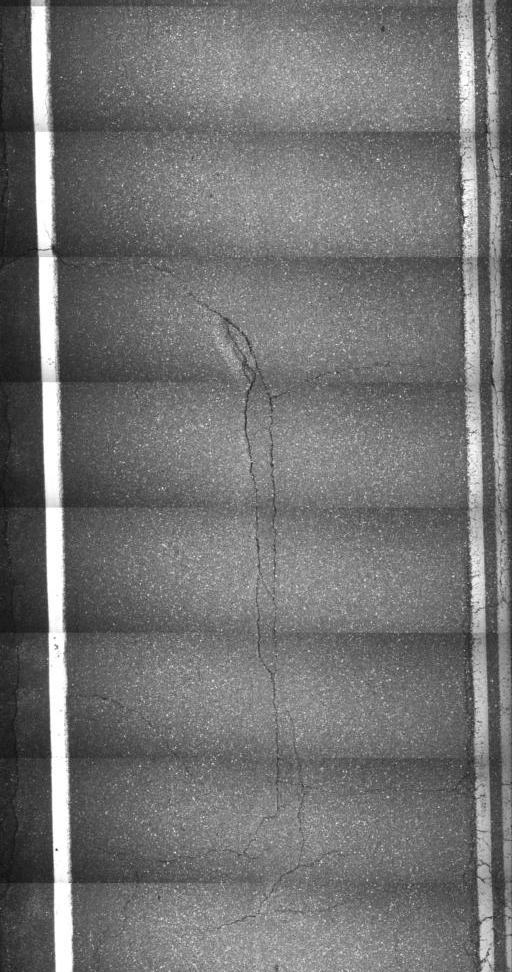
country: US
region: Vermont
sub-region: Windsor County
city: Woodstock
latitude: 43.5393
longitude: -72.7181
